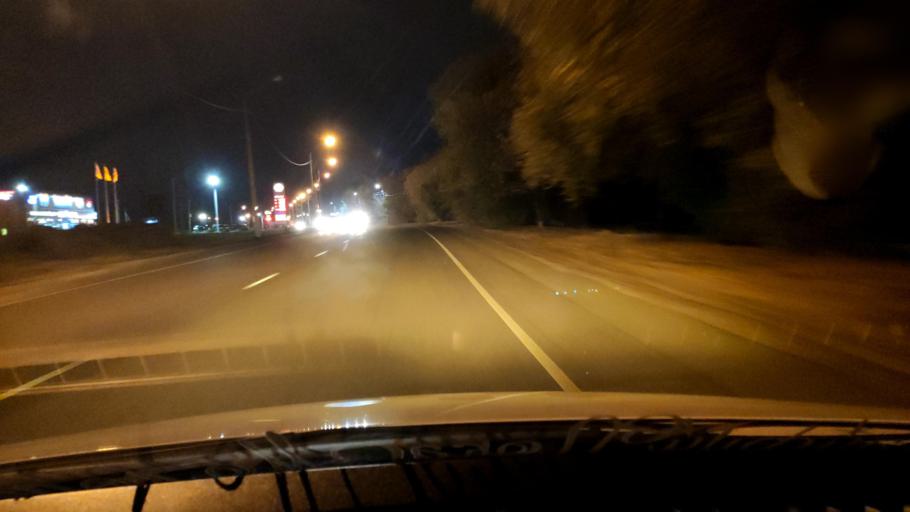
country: RU
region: Voronezj
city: Voronezh
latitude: 51.6142
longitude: 39.1790
